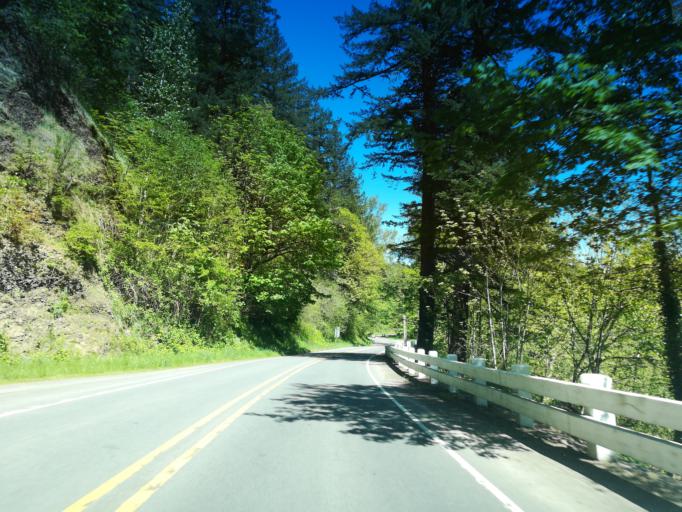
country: US
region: Oregon
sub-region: Multnomah County
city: Troutdale
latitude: 45.5163
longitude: -122.3607
